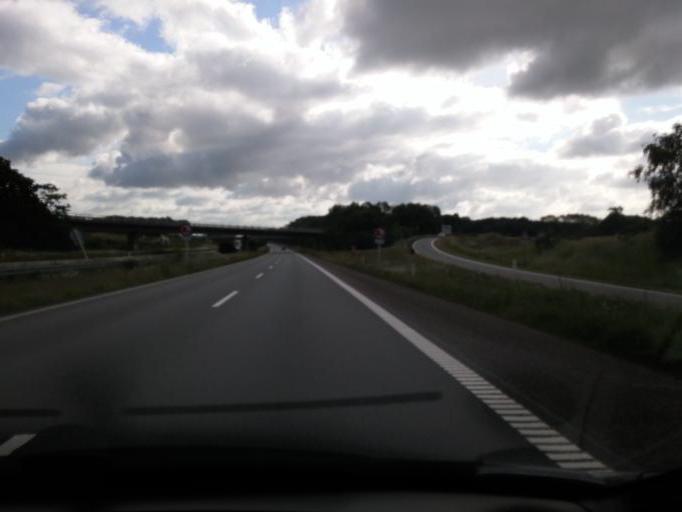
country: DK
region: Zealand
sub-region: Koge Kommune
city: Ejby
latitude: 55.4689
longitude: 12.0664
